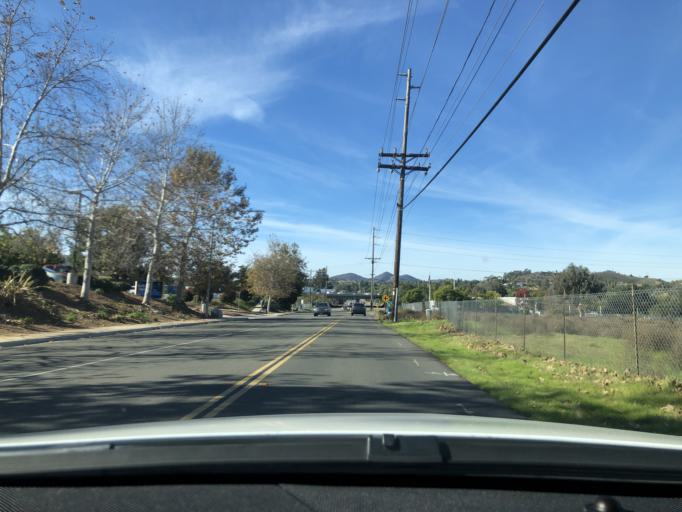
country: US
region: California
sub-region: San Diego County
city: Escondido
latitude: 33.0917
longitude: -117.0784
